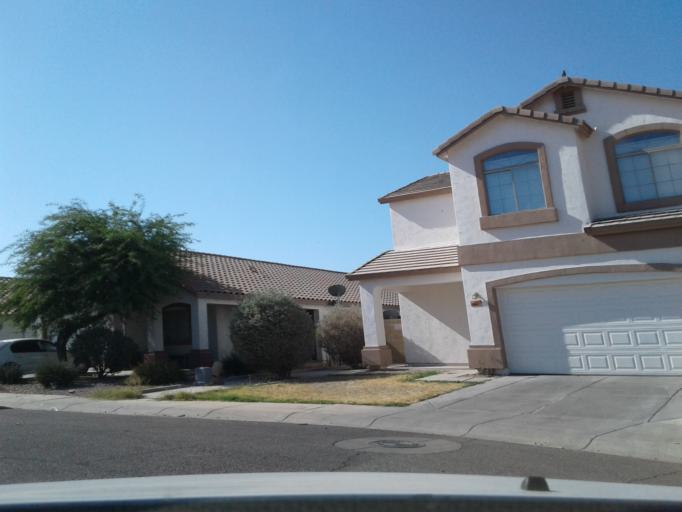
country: US
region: Arizona
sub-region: Maricopa County
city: Laveen
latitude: 33.4113
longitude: -112.1908
